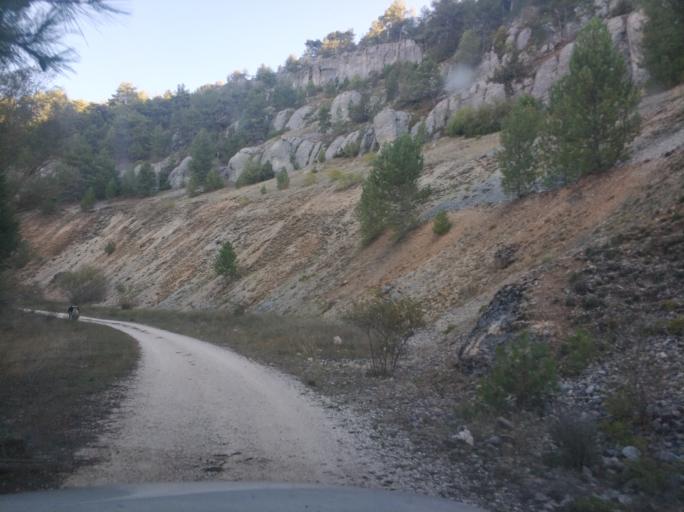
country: ES
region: Castille and Leon
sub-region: Provincia de Burgos
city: Hontoria del Pinar
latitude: 41.8414
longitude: -3.1610
